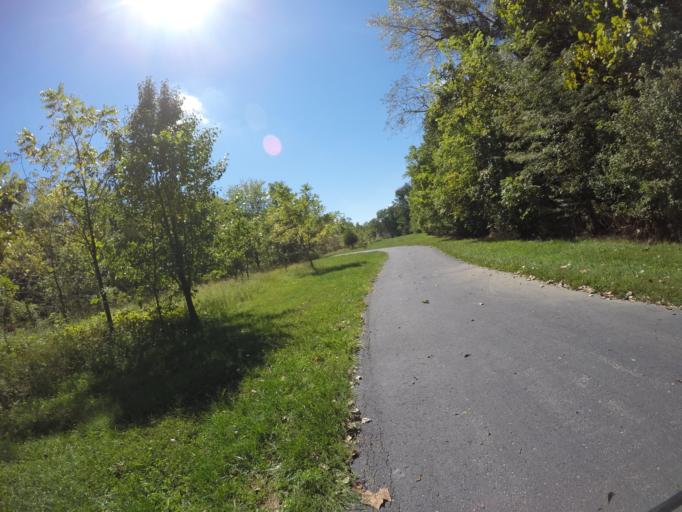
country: US
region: Kansas
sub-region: Johnson County
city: Lenexa
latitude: 38.9080
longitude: -94.7307
